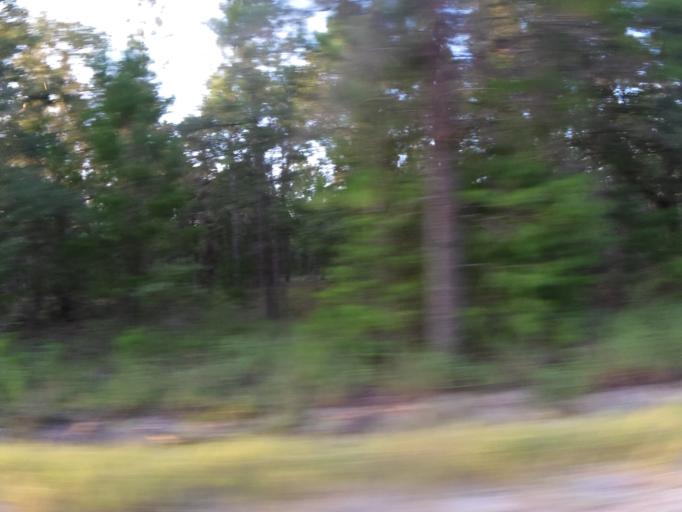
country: US
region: Florida
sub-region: Baker County
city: Macclenny
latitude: 30.3937
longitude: -82.1031
